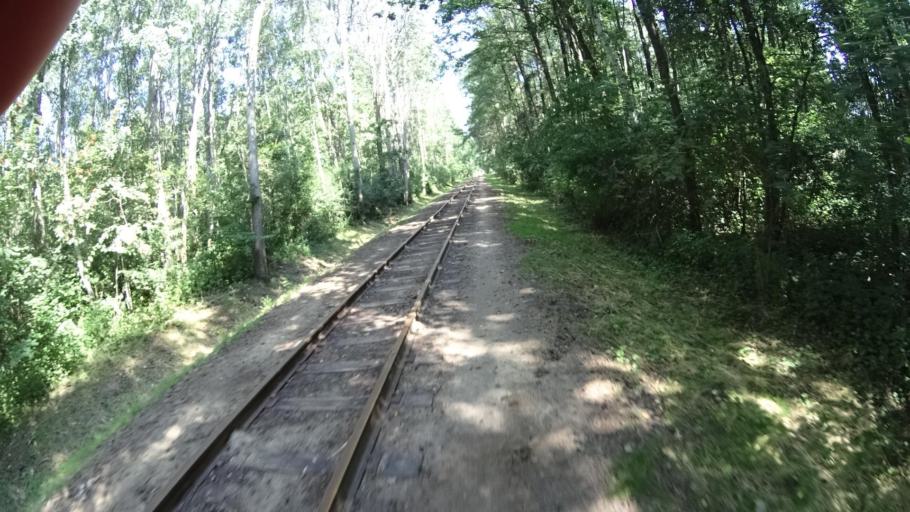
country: PL
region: Masovian Voivodeship
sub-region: Powiat piaseczynski
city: Tarczyn
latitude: 51.9887
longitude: 20.8858
